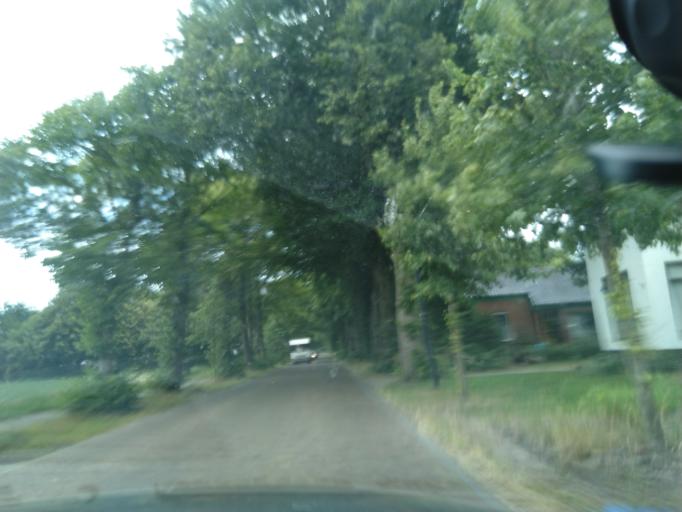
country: NL
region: Groningen
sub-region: Gemeente Vlagtwedde
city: Vlagtwedde
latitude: 53.0791
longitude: 7.1227
